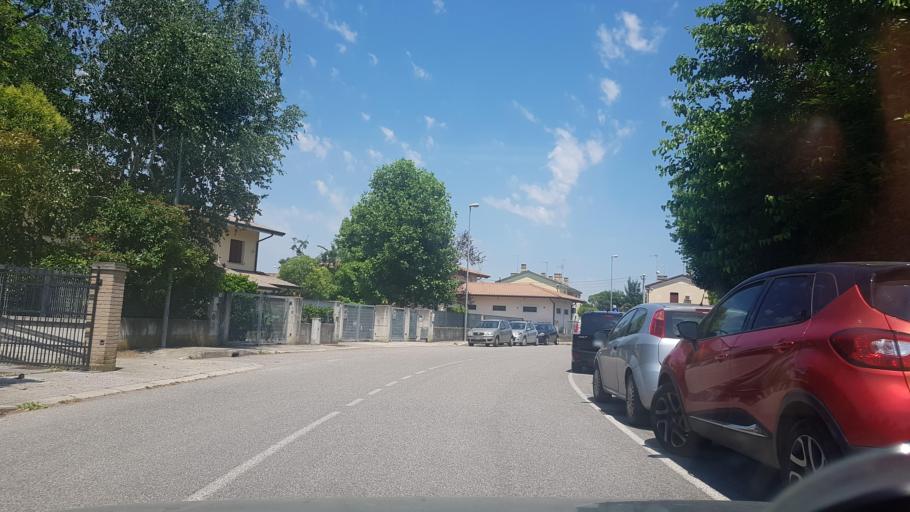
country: IT
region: Friuli Venezia Giulia
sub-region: Provincia di Gorizia
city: Turriaco
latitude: 45.8206
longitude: 13.4421
